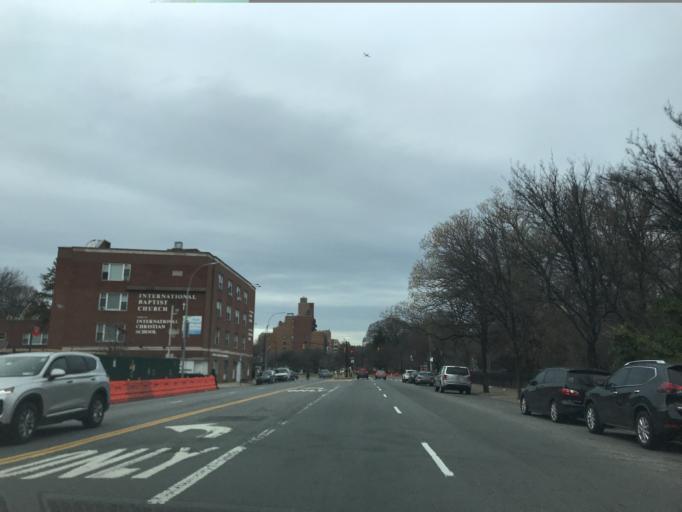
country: US
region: New York
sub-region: Kings County
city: Brooklyn
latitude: 40.6495
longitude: -73.9717
